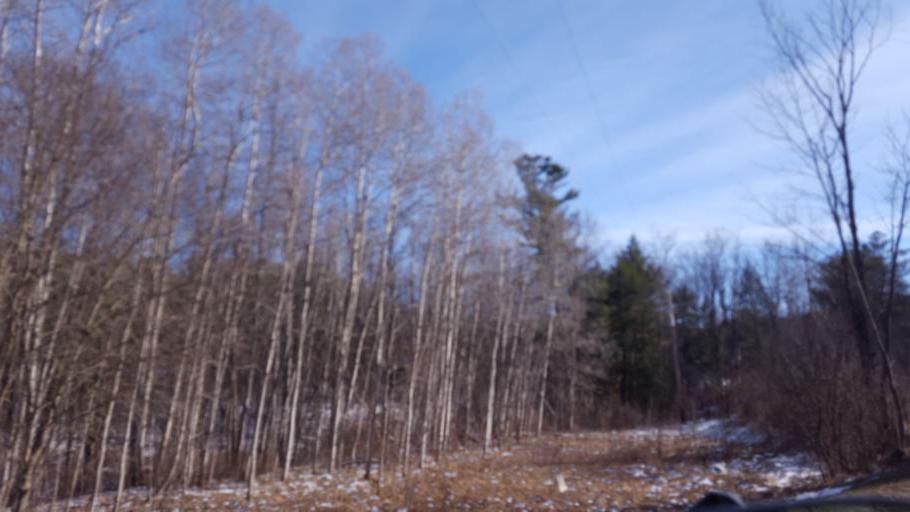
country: US
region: New York
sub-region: Allegany County
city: Wellsville
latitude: 42.0920
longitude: -77.9874
